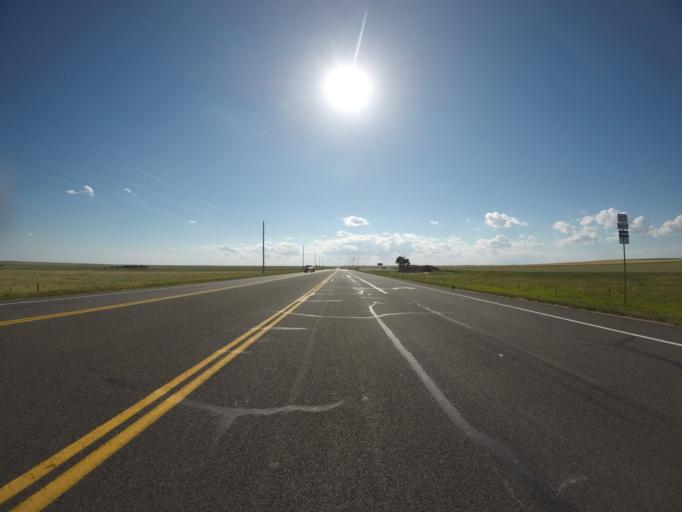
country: US
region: Colorado
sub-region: Morgan County
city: Brush
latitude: 40.6101
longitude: -103.6738
